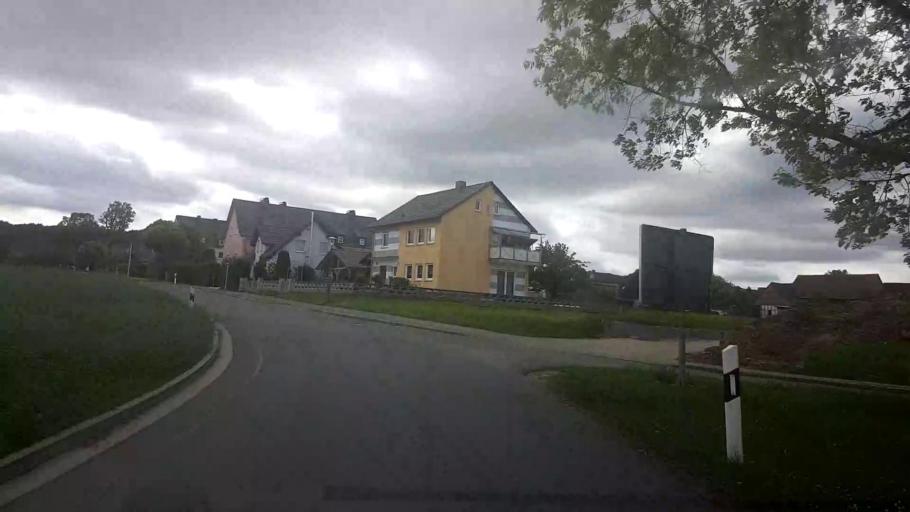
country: DE
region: Bavaria
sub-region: Upper Franconia
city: Lichtenfels
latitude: 50.1242
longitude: 11.0363
